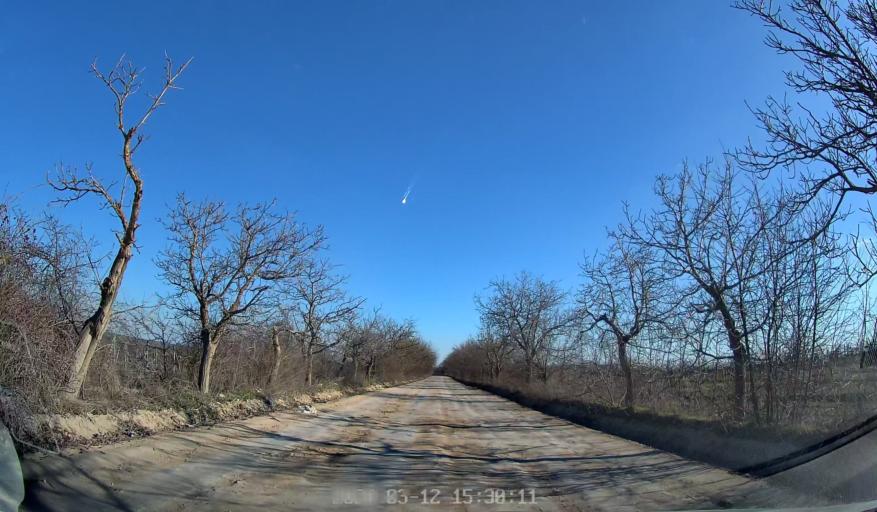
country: MD
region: Chisinau
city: Ciorescu
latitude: 47.1618
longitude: 28.9379
